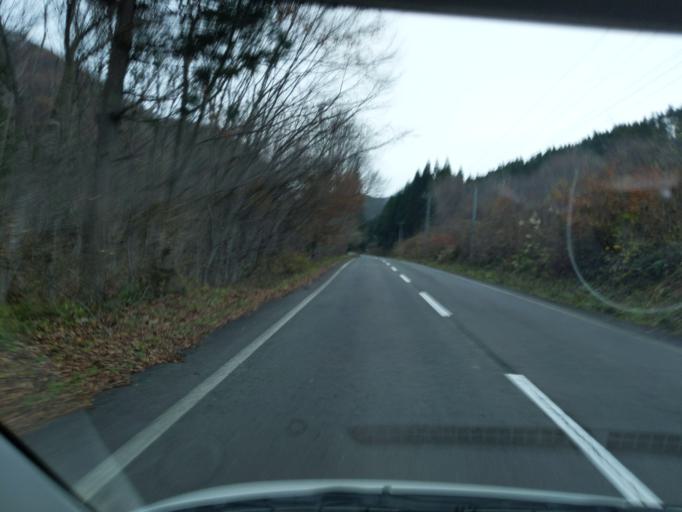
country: JP
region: Iwate
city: Tono
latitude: 39.1843
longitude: 141.3572
